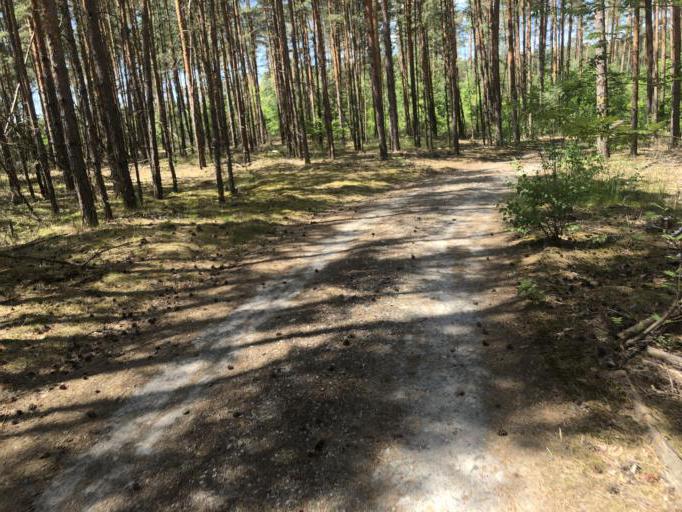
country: DE
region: Brandenburg
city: Gross Koris
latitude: 52.1947
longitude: 13.6496
